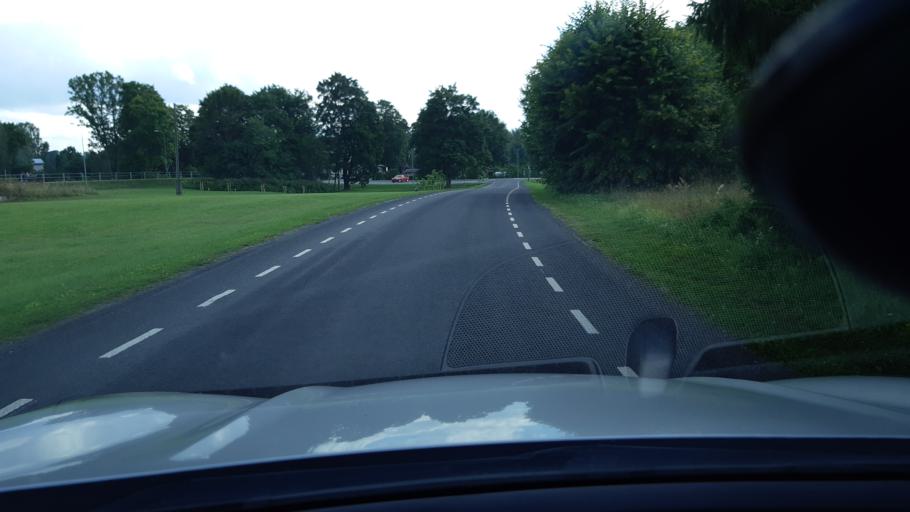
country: EE
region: Raplamaa
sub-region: Kehtna vald
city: Kehtna
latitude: 58.9435
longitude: 24.8968
